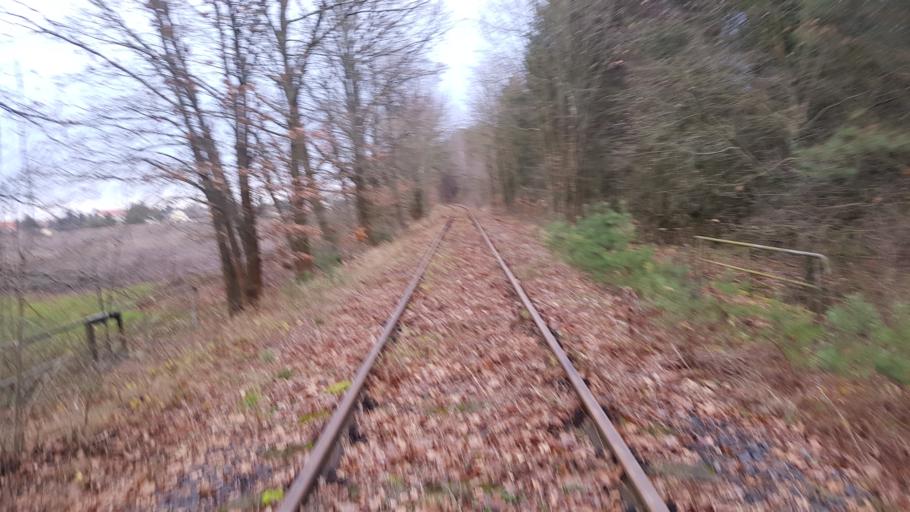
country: DE
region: Brandenburg
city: Finsterwalde
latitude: 51.6180
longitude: 13.7496
